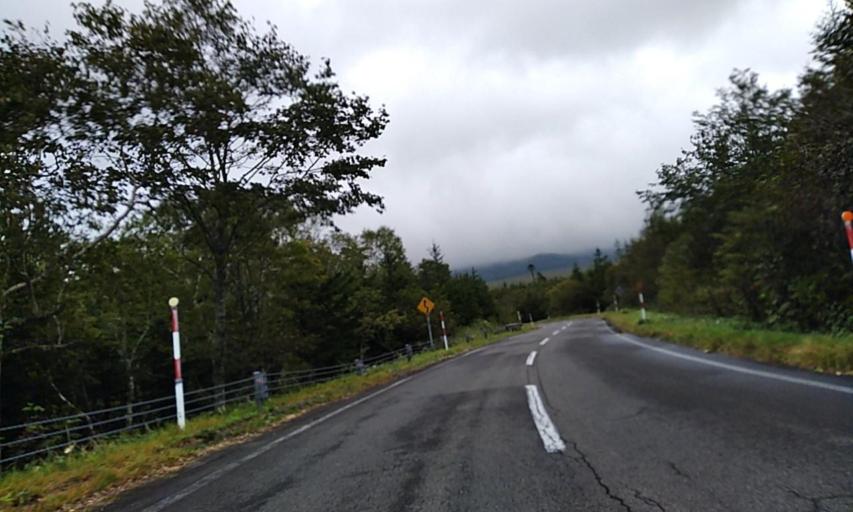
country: JP
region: Hokkaido
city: Abashiri
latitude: 43.6055
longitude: 144.5857
